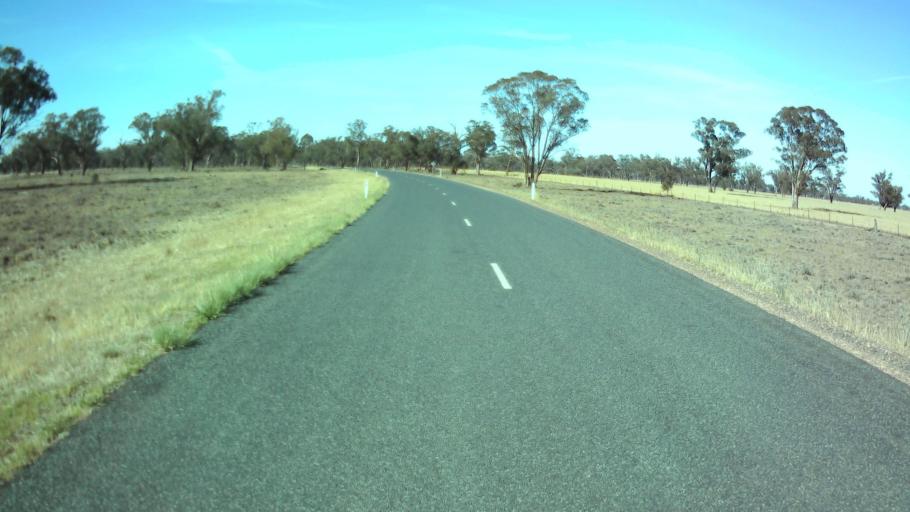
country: AU
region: New South Wales
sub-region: Weddin
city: Grenfell
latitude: -34.0583
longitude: 147.9116
